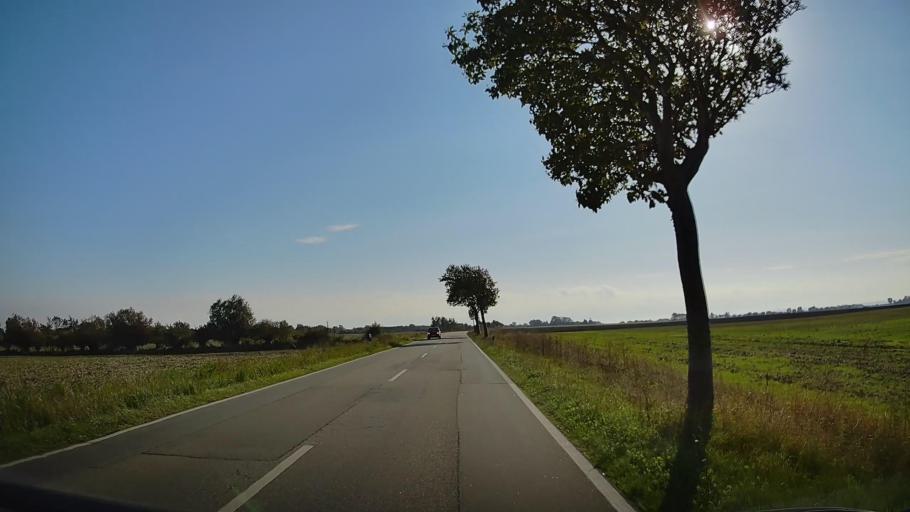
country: DE
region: Schleswig-Holstein
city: Fehmarn
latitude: 54.4367
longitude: 11.1367
